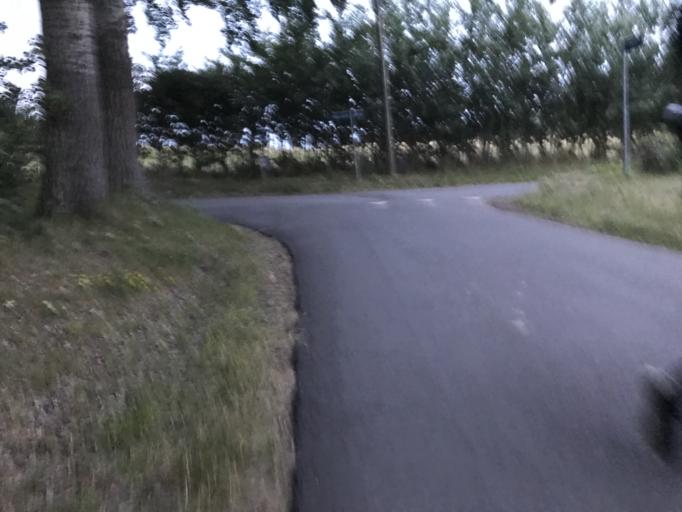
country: DK
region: South Denmark
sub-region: Faaborg-Midtfyn Kommune
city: Faaborg
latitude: 54.9346
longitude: 10.2482
